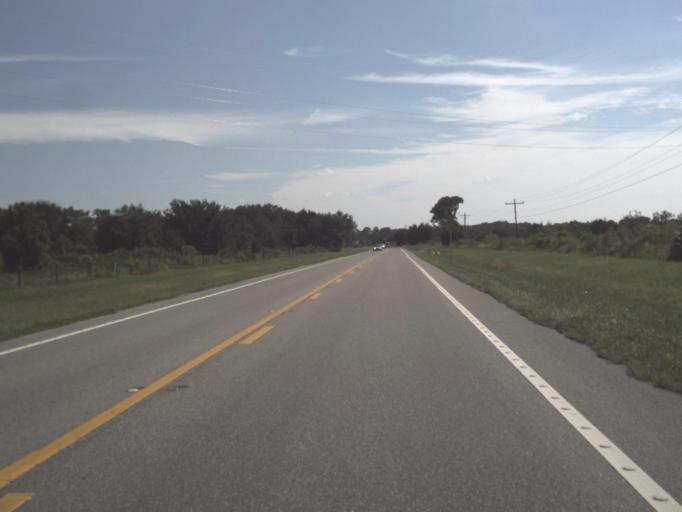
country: US
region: Florida
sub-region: Highlands County
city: Avon Park
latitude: 27.5921
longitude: -81.5709
